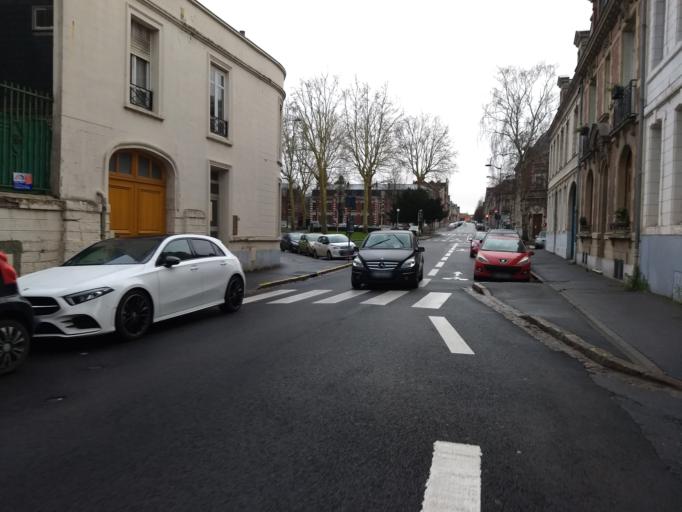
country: FR
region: Nord-Pas-de-Calais
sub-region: Departement du Pas-de-Calais
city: Arras
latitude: 50.2883
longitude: 2.7704
